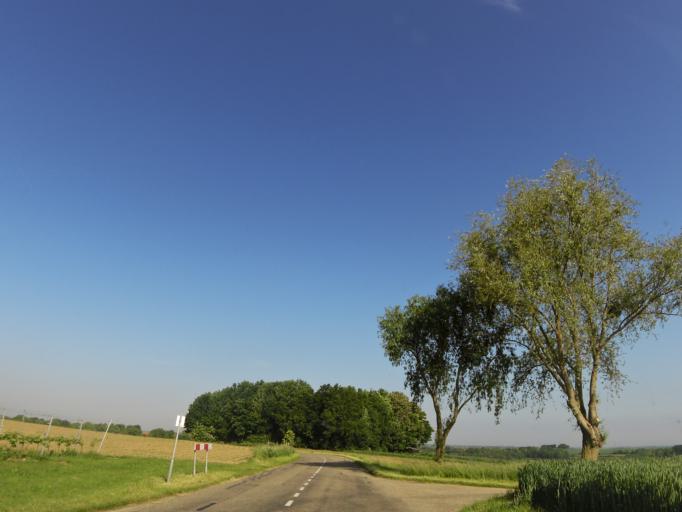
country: NL
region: Limburg
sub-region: Gemeente Voerendaal
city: Ubachsberg
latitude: 50.8401
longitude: 5.9299
